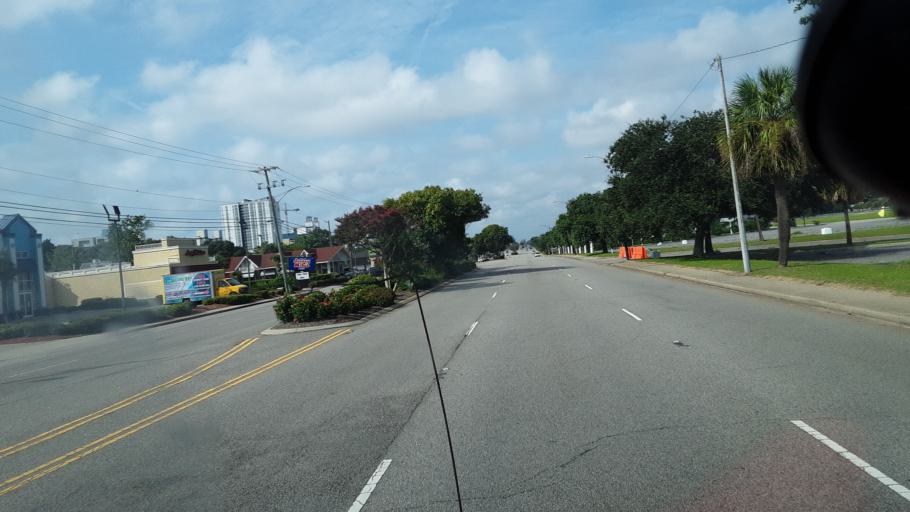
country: US
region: South Carolina
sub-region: Horry County
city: Myrtle Beach
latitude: 33.7079
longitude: -78.8659
